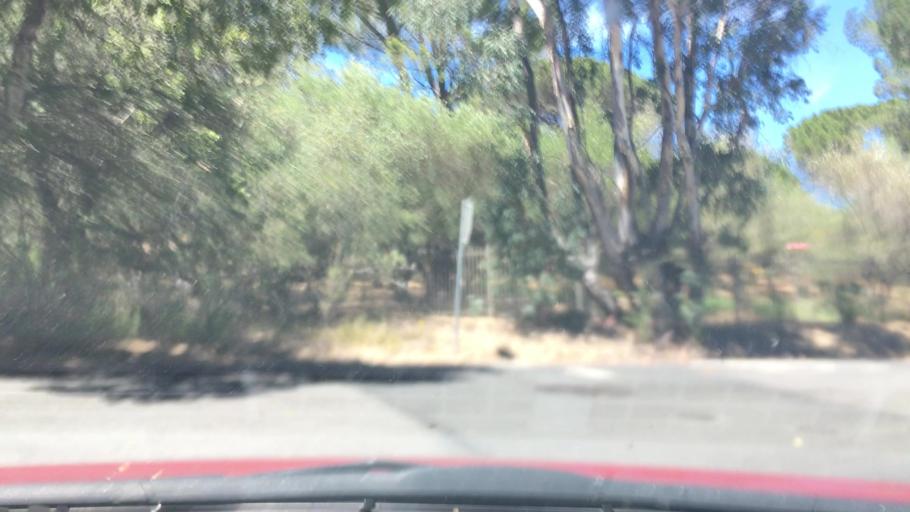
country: US
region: California
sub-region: San Mateo County
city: Woodside
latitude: 37.4363
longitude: -122.2696
